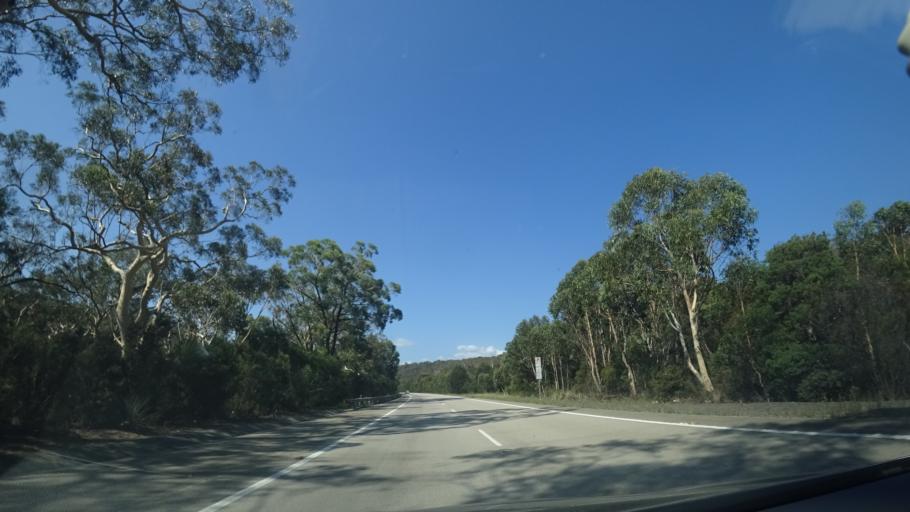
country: AU
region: New South Wales
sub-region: Wingecarribee
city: Mittagong
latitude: -34.4303
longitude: 150.4625
